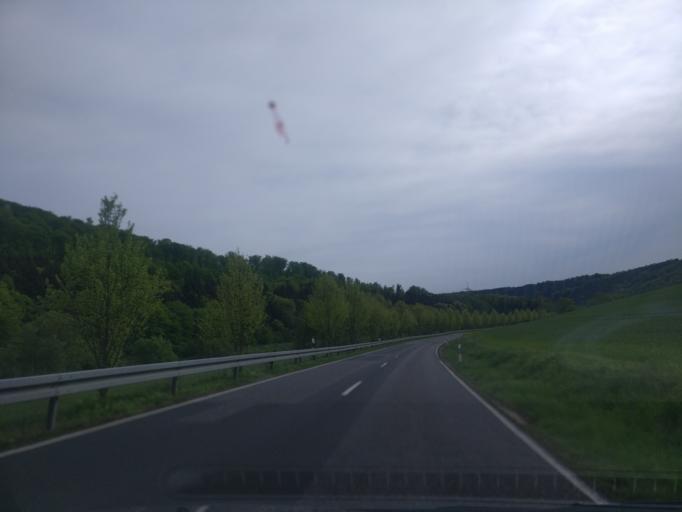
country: DE
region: Hesse
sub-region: Regierungsbezirk Kassel
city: Fuldatal
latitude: 51.3935
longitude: 9.5732
